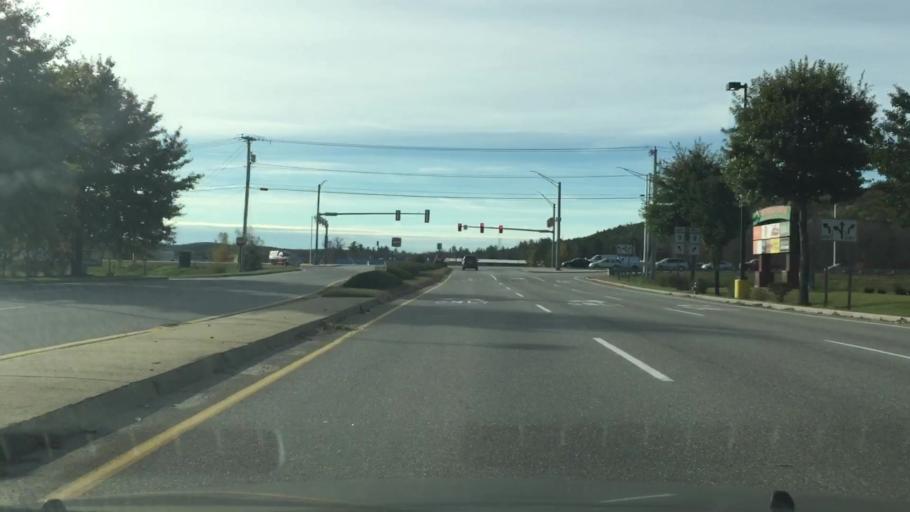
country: US
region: New Hampshire
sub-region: Cheshire County
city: Keene
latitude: 42.9246
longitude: -72.3060
